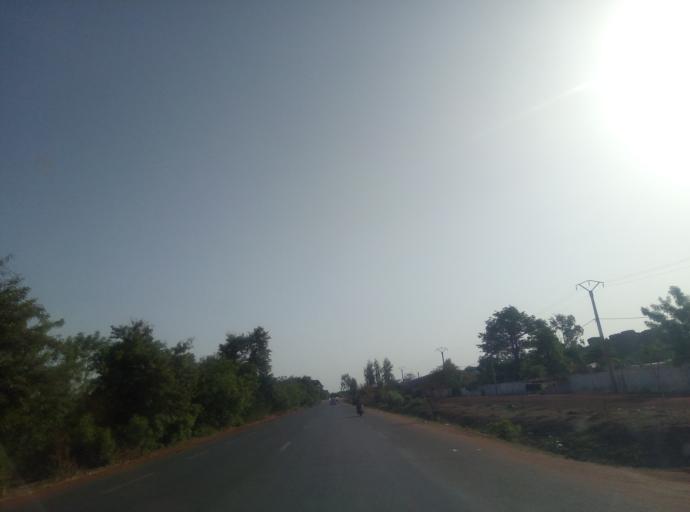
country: ML
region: Bamako
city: Bamako
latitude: 12.5842
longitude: -7.7714
